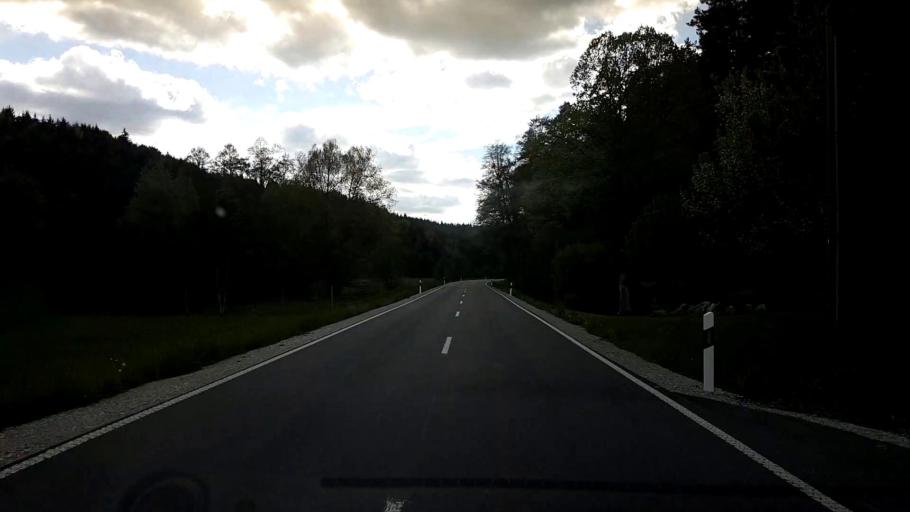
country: DE
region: Bavaria
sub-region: Upper Franconia
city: Hollfeld
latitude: 49.9531
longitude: 11.2693
